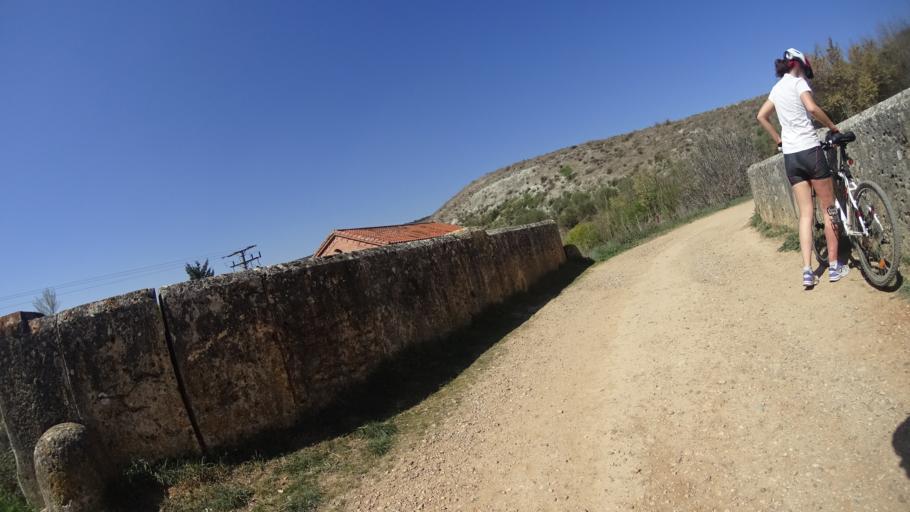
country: ES
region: Castille and Leon
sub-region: Provincia de Palencia
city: Villamuriel de Cerrato
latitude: 41.9214
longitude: -4.5246
